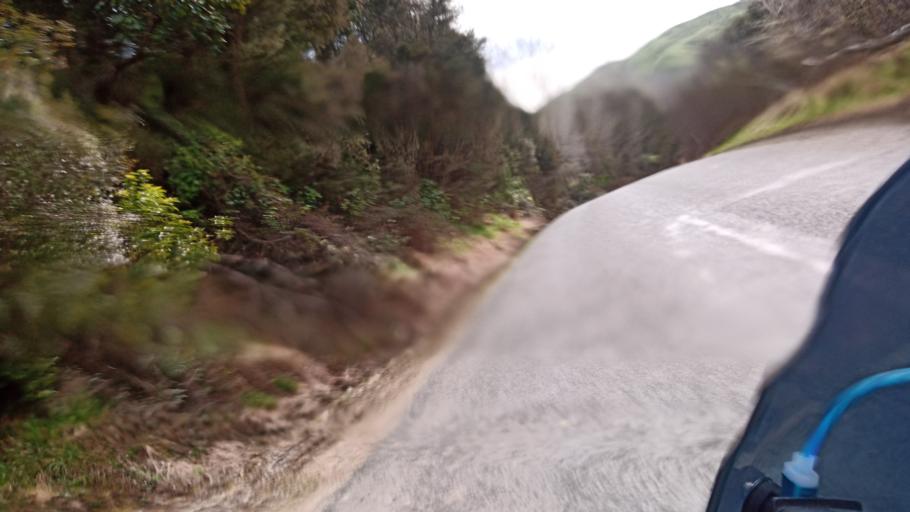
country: NZ
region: Hawke's Bay
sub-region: Wairoa District
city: Wairoa
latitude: -38.8029
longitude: 177.4709
